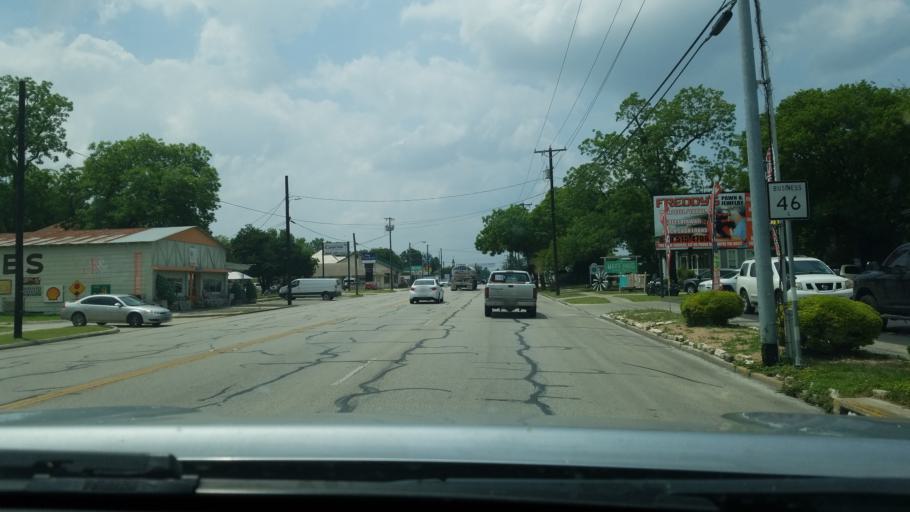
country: US
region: Texas
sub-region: Comal County
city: New Braunfels
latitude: 29.6973
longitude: -98.1162
